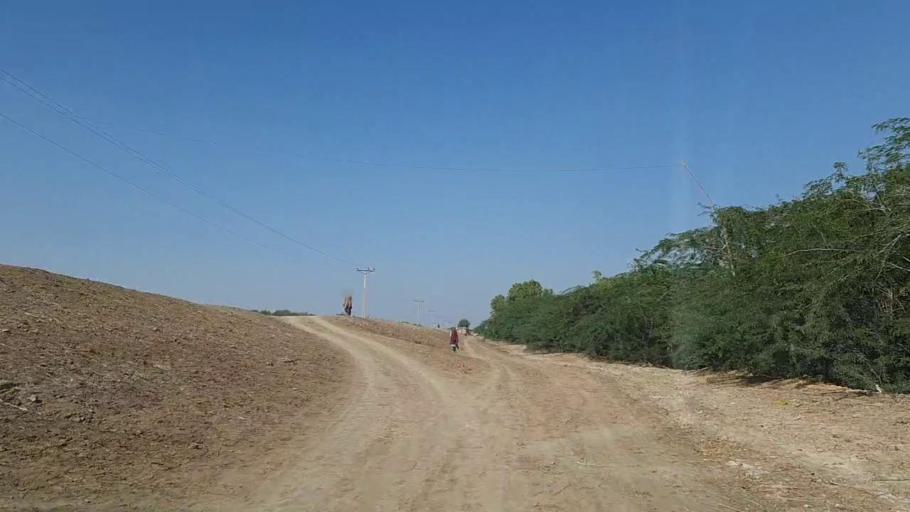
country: PK
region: Sindh
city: Chuhar Jamali
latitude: 24.5449
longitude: 68.0156
